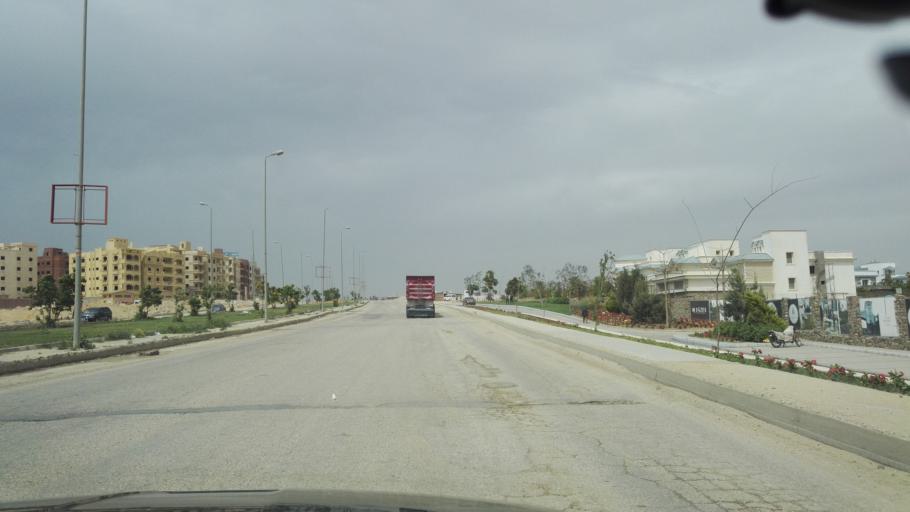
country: EG
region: Muhafazat al Qalyubiyah
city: Al Khankah
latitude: 30.0321
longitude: 31.5288
